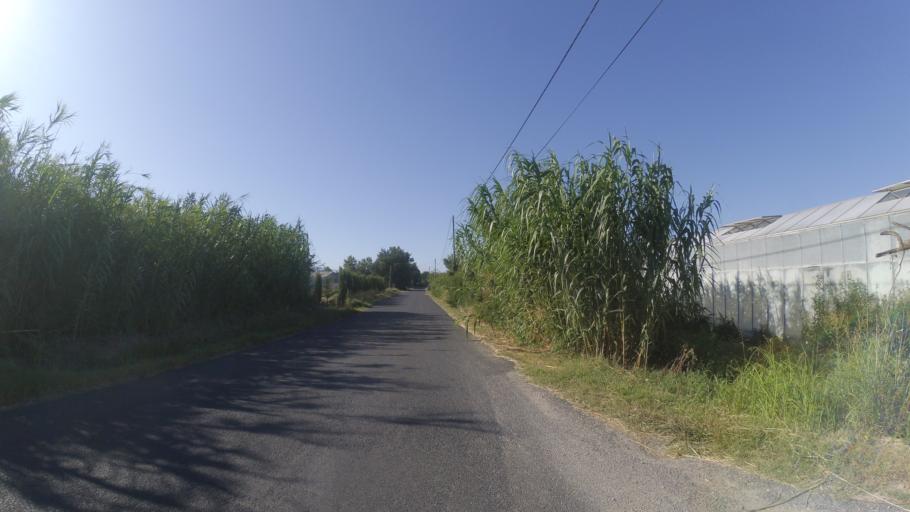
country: FR
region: Languedoc-Roussillon
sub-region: Departement des Pyrenees-Orientales
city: Villeneuve-la-Riviere
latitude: 42.7005
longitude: 2.7992
